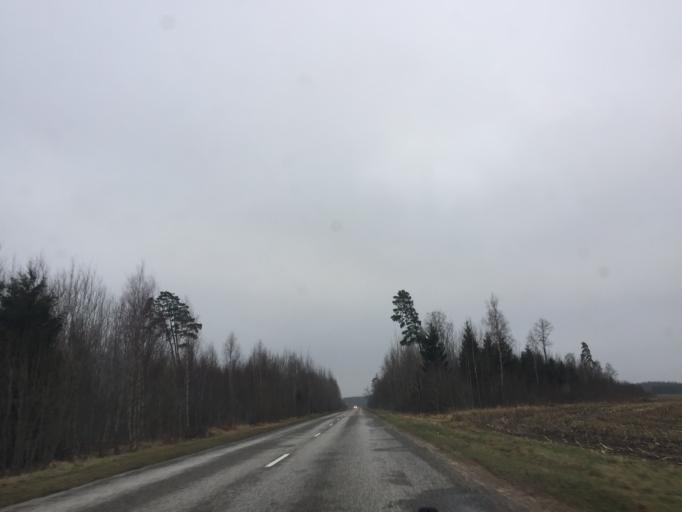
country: LV
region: Limbazu Rajons
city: Limbazi
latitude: 57.5593
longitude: 24.6683
